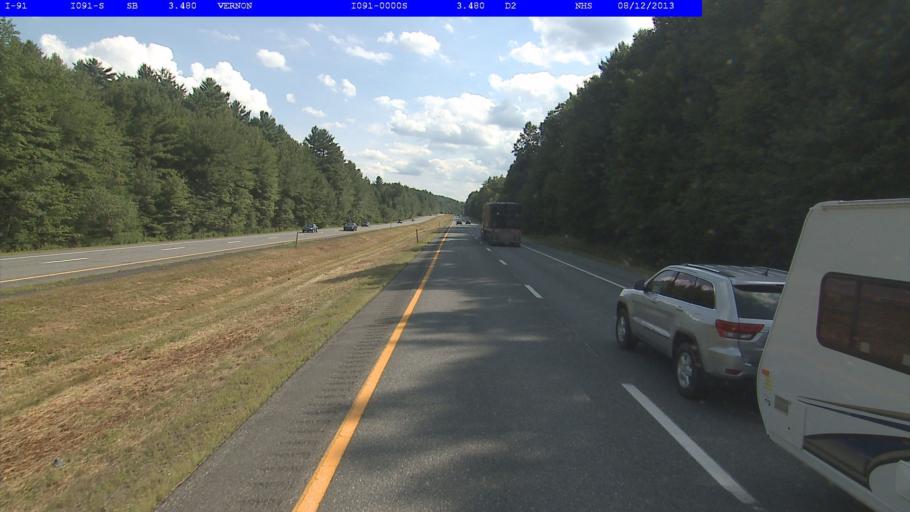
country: US
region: Vermont
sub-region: Windham County
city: Brattleboro
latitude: 42.7798
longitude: -72.5610
